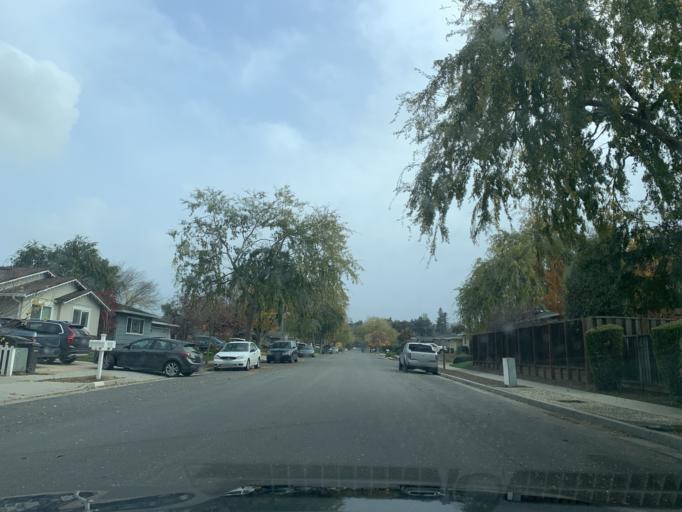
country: US
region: California
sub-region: Santa Clara County
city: Monte Sereno
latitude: 37.2664
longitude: -121.9893
